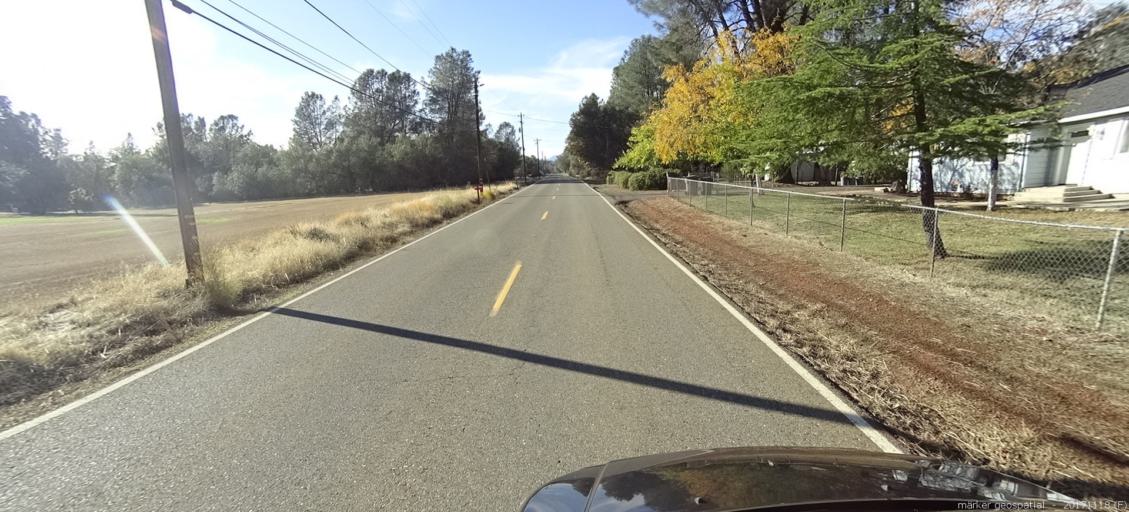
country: US
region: California
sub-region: Shasta County
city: Redding
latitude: 40.4780
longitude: -122.4442
